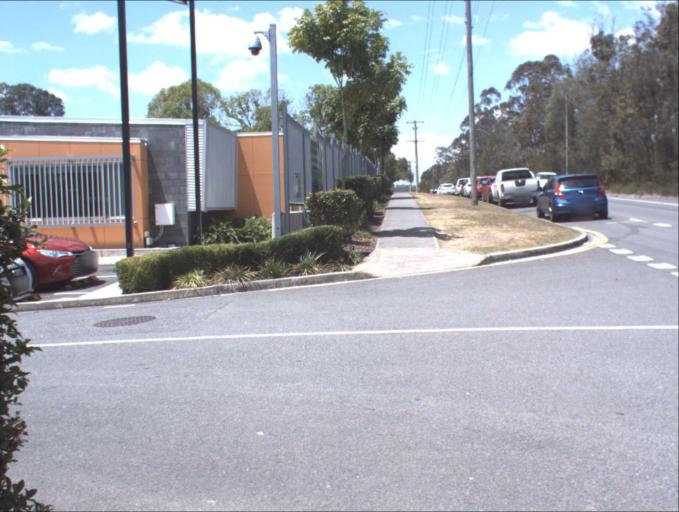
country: AU
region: Queensland
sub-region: Logan
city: Waterford West
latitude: -27.6714
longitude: 153.1423
